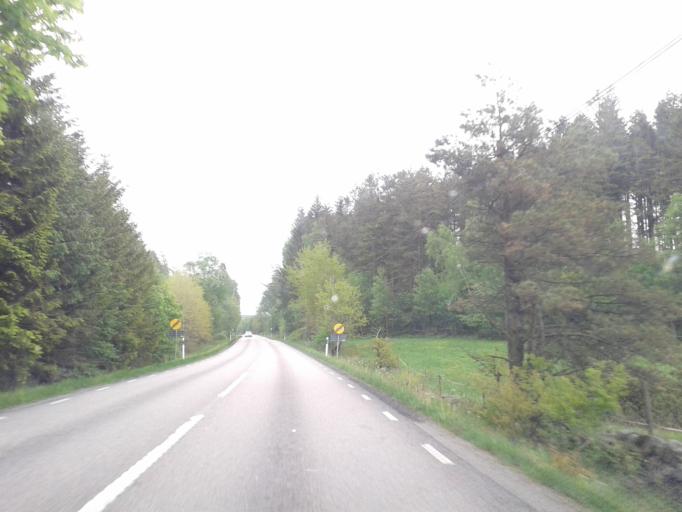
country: SE
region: Vaestra Goetaland
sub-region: Kungalvs Kommun
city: Kode
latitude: 57.8925
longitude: 11.8615
